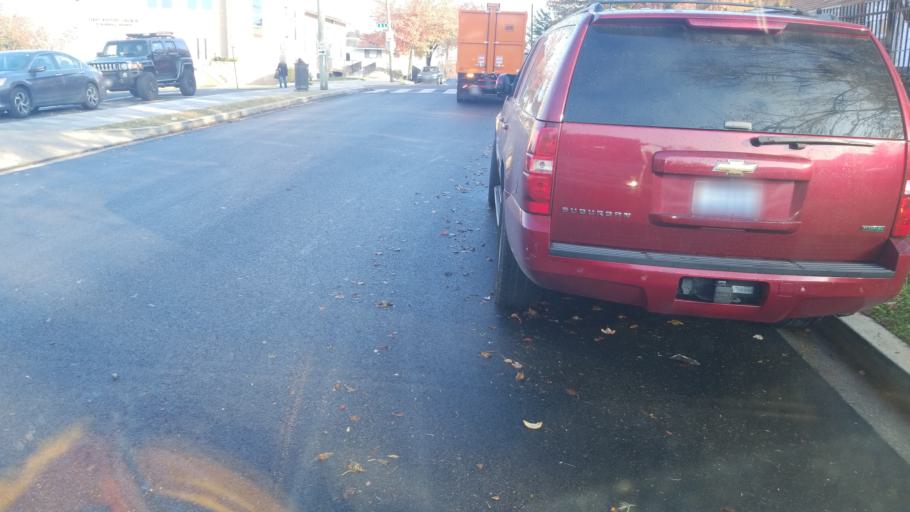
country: US
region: Maryland
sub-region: Prince George's County
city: Capitol Heights
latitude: 38.8863
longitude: -76.9304
